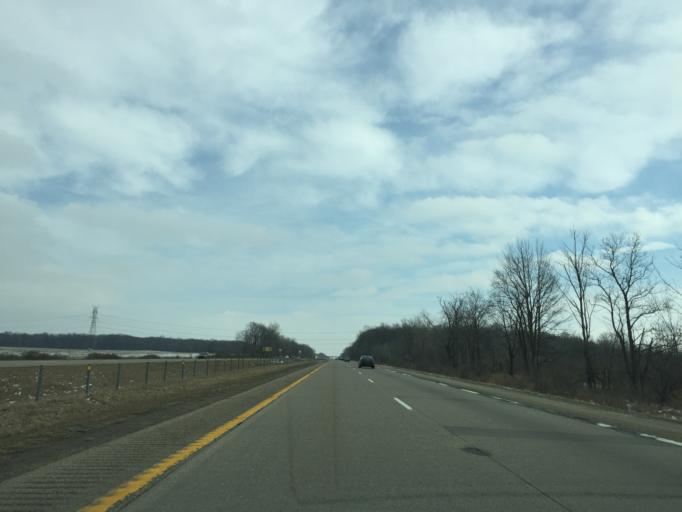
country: US
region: Michigan
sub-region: Kent County
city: Forest Hills
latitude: 42.8783
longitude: -85.4323
